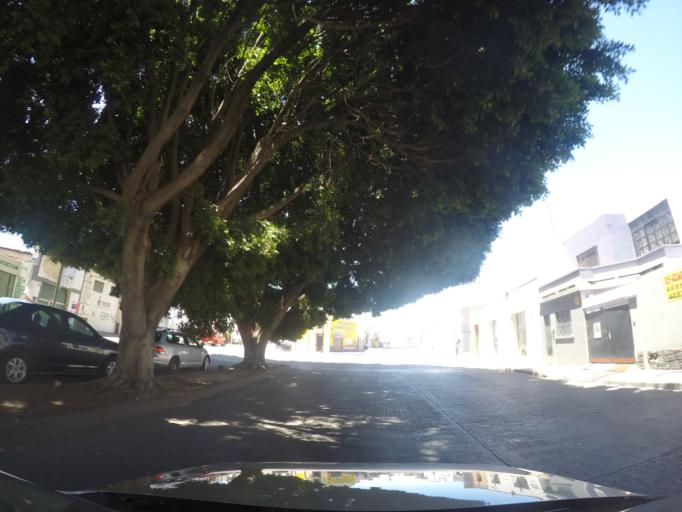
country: MX
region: San Luis Potosi
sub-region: San Luis Potosi
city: San Luis Potosi
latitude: 22.1548
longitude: -100.9815
